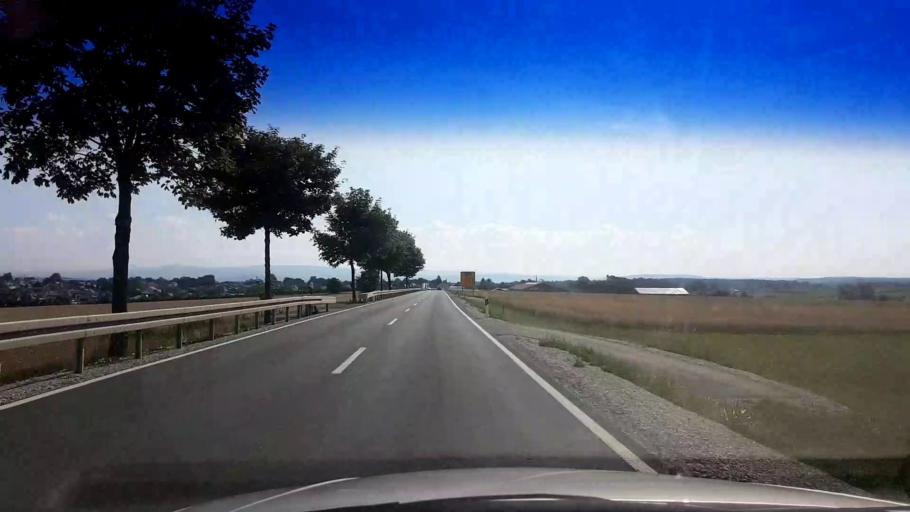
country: DE
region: Bavaria
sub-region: Upper Franconia
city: Eckersdorf
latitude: 49.9307
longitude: 11.4827
